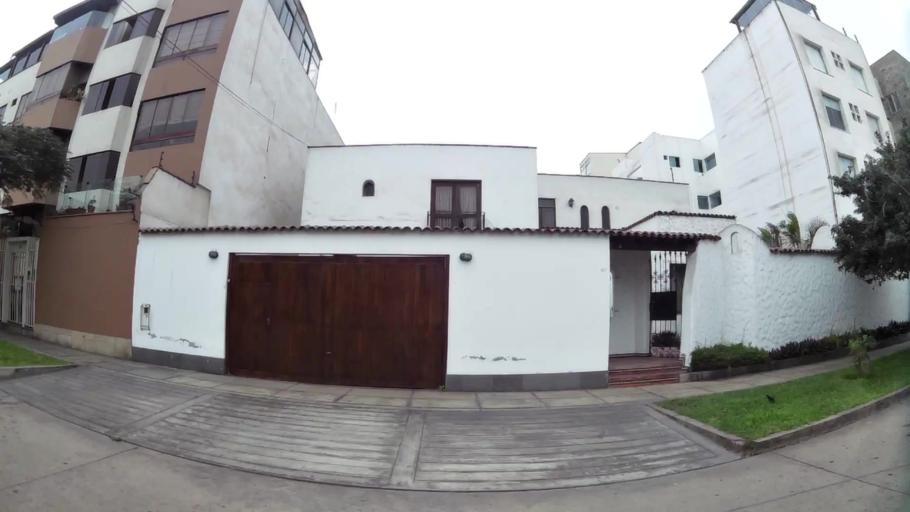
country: PE
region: Lima
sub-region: Lima
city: Surco
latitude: -12.1185
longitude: -76.9879
